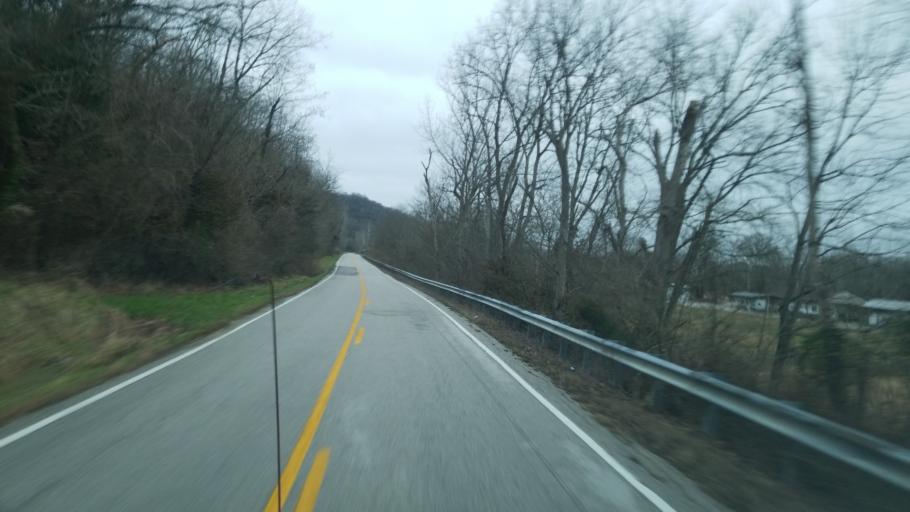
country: US
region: Kentucky
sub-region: Bracken County
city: Brooksville
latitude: 38.7719
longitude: -84.1114
